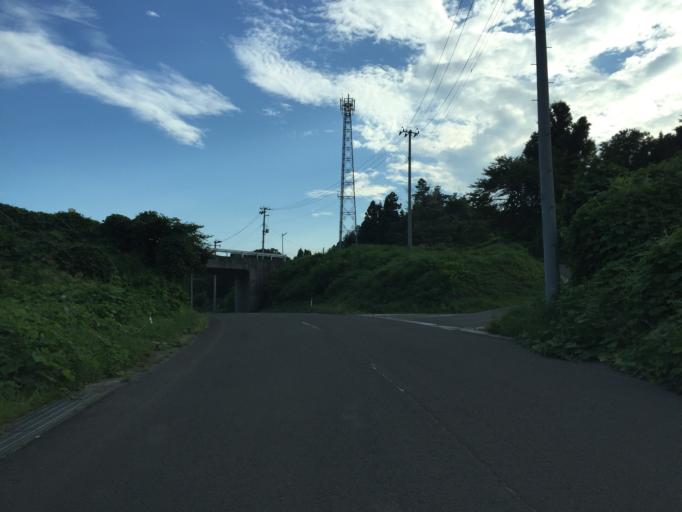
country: JP
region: Fukushima
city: Fukushima-shi
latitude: 37.6566
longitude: 140.5682
